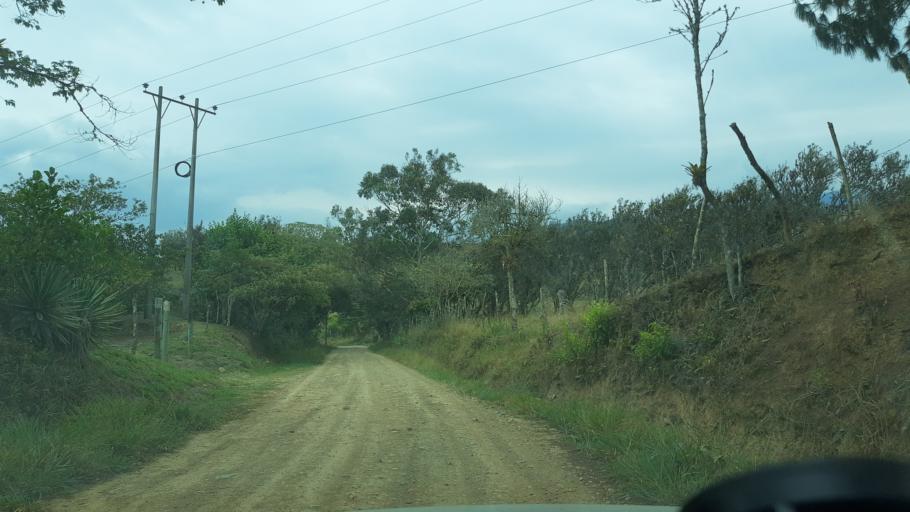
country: CO
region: Boyaca
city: Somondoco
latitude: 4.9913
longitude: -73.3740
